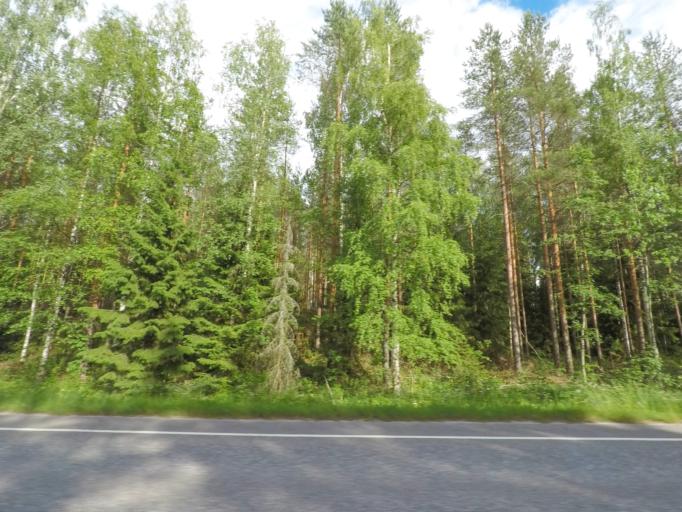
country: FI
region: Paijanne Tavastia
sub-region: Lahti
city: Hollola
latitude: 60.8167
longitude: 25.4833
